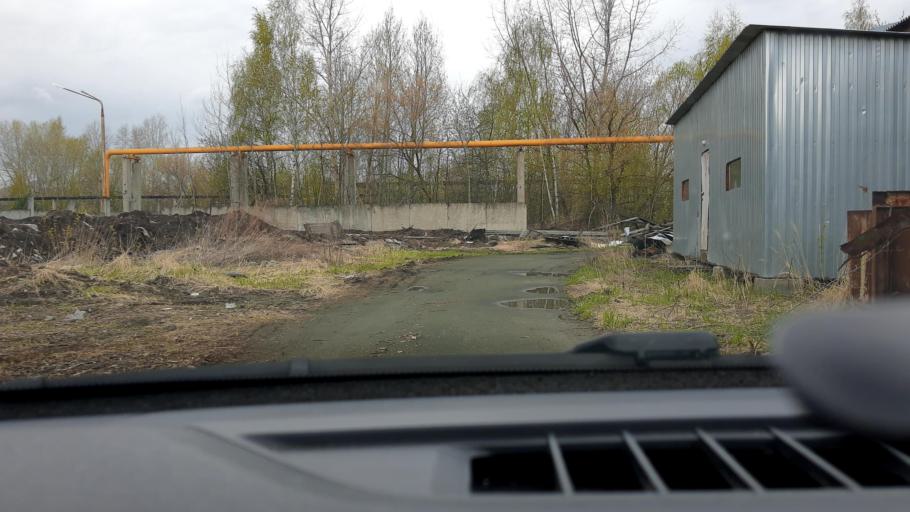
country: RU
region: Nizjnij Novgorod
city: Nizhniy Novgorod
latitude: 56.2462
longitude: 43.9162
